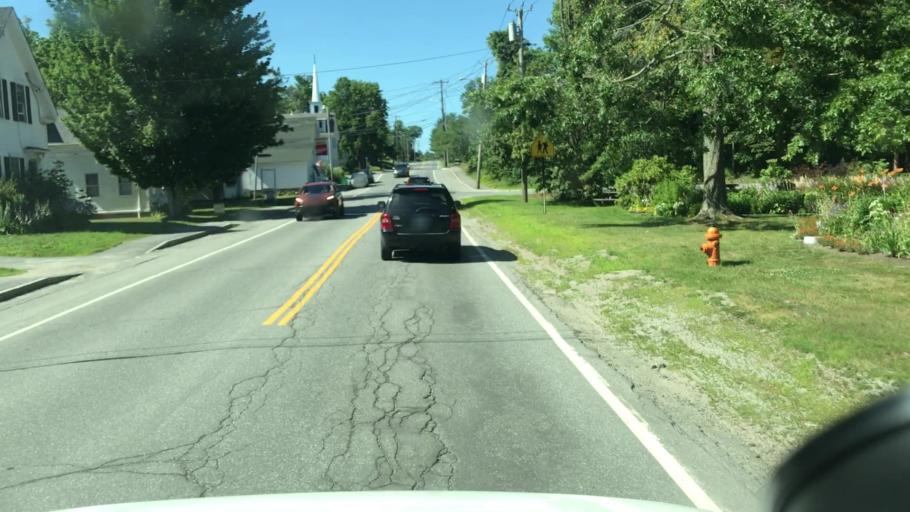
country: US
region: Maine
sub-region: Hancock County
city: Ellsworth
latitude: 44.5449
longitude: -68.4255
